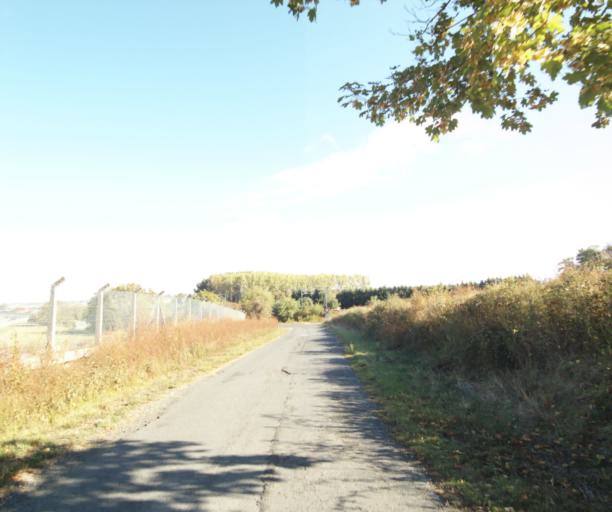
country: FR
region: Auvergne
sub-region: Departement du Puy-de-Dome
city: Gerzat
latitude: 45.8411
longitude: 3.1414
